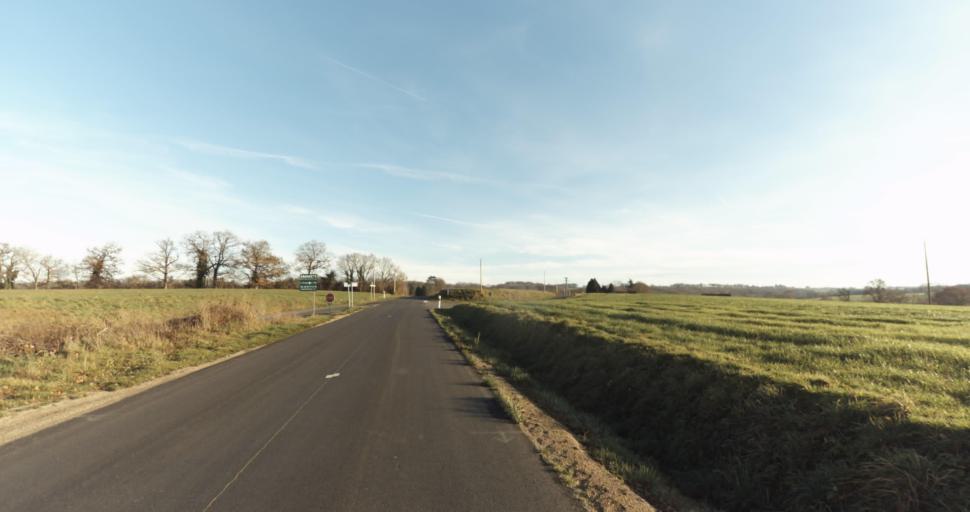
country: FR
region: Limousin
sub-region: Departement de la Haute-Vienne
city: Aixe-sur-Vienne
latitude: 45.7857
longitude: 1.1538
